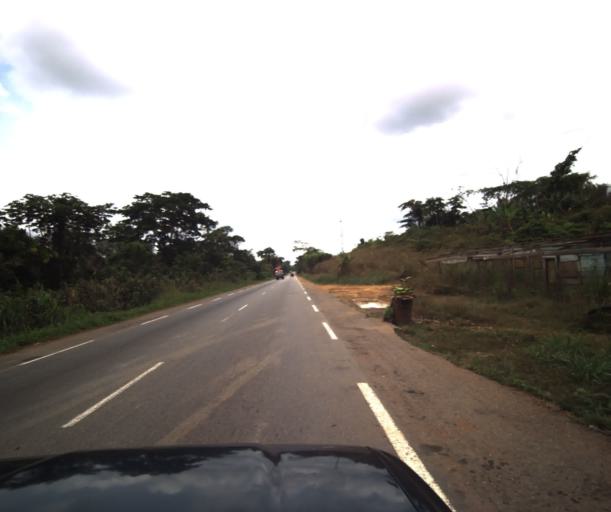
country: CM
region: Centre
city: Eseka
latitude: 3.8416
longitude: 10.9795
